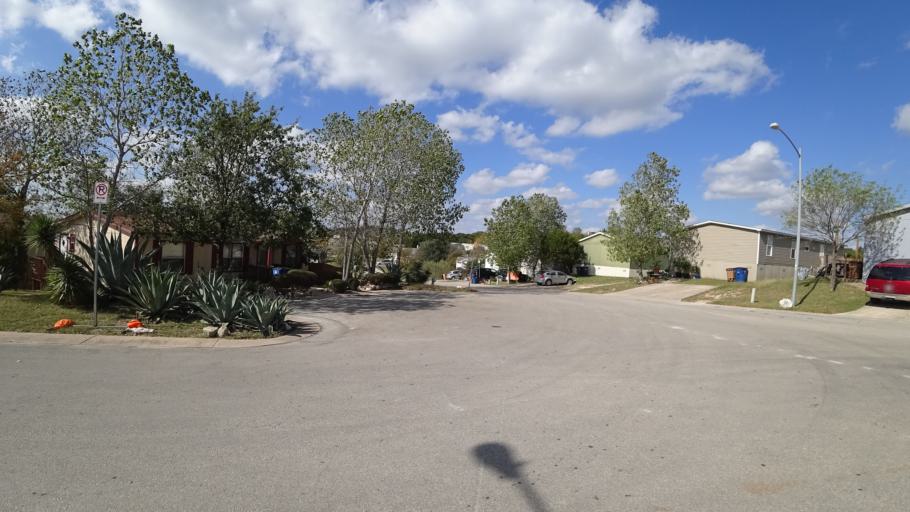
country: US
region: Texas
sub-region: Travis County
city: Barton Creek
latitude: 30.2500
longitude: -97.8826
